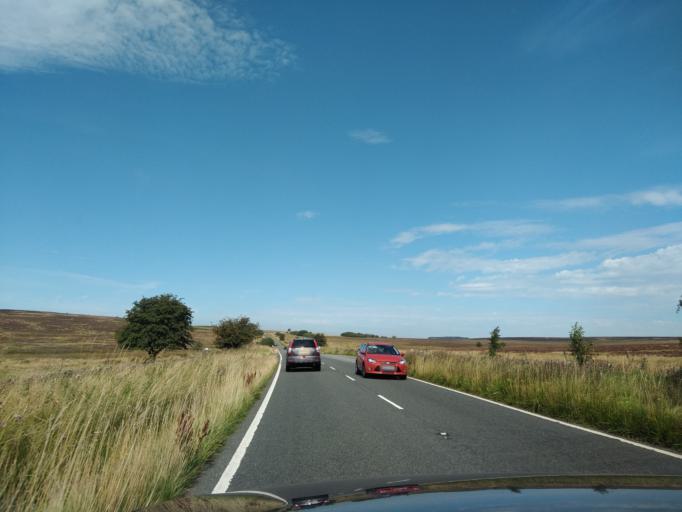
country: GB
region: England
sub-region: Derbyshire
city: Hathersage
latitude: 53.2989
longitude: -1.5845
